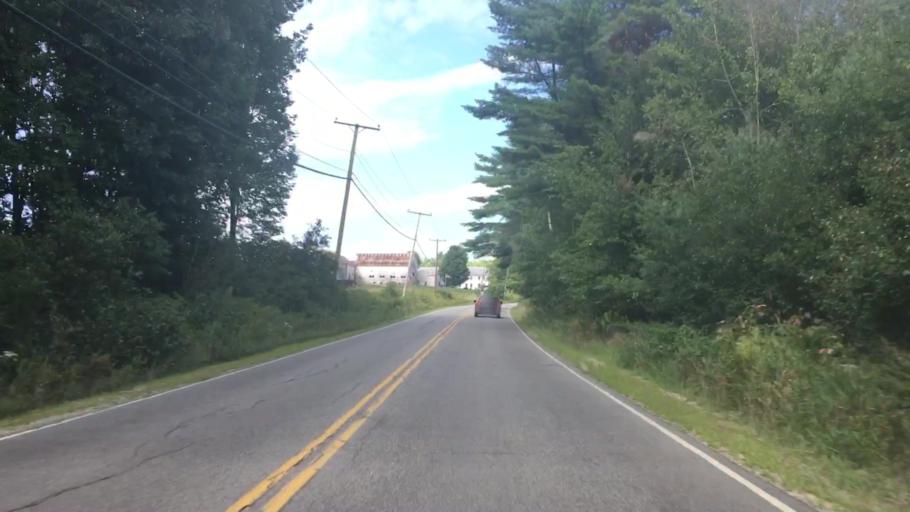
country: US
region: Maine
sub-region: Oxford County
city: Oxford
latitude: 44.1273
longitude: -70.5043
